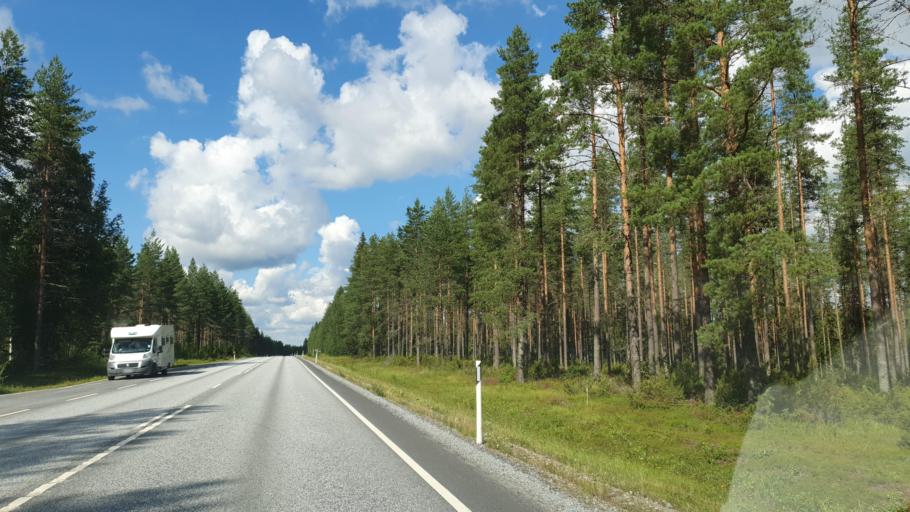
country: FI
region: Northern Savo
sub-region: Ylae-Savo
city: Sonkajaervi
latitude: 63.8939
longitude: 27.4148
